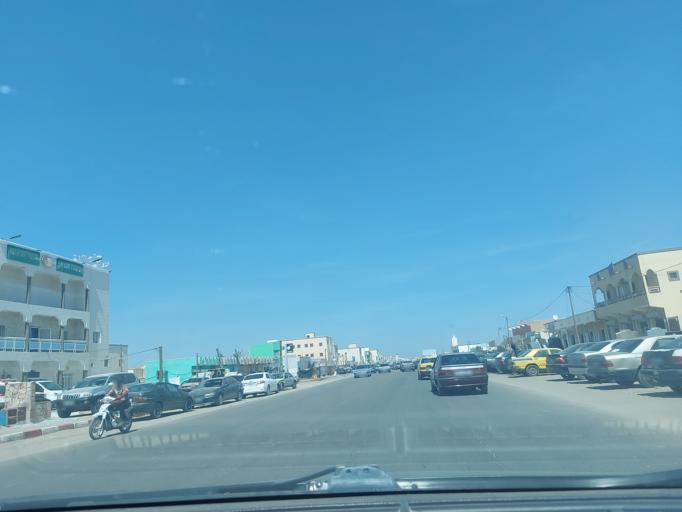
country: MR
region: Nouakchott
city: Nouakchott
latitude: 18.0754
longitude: -15.9515
